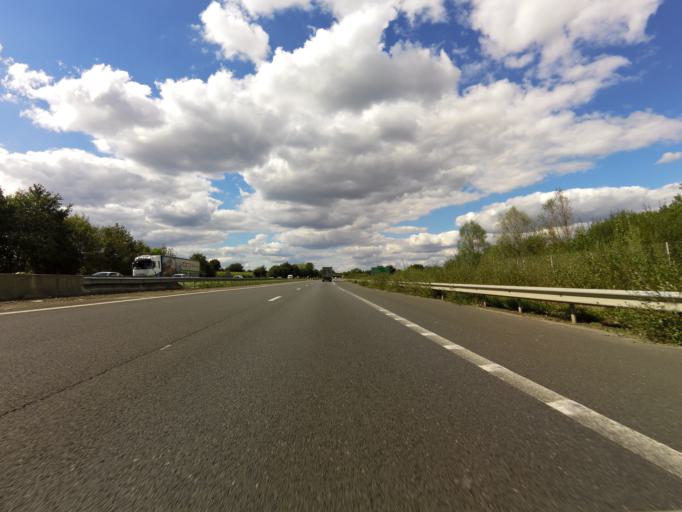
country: FR
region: Pays de la Loire
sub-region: Departement de la Loire-Atlantique
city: Sautron
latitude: 47.2653
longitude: -1.7081
